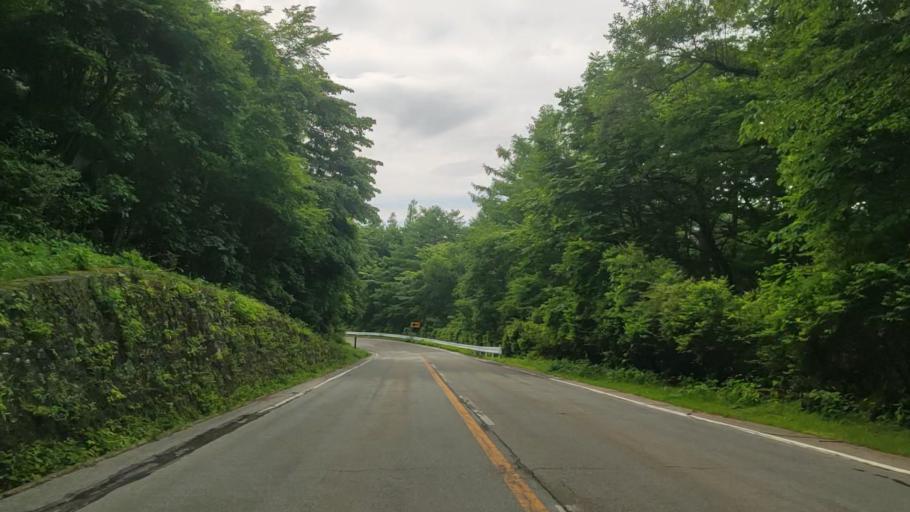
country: JP
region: Yamanashi
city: Fujikawaguchiko
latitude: 35.4212
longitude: 138.7393
